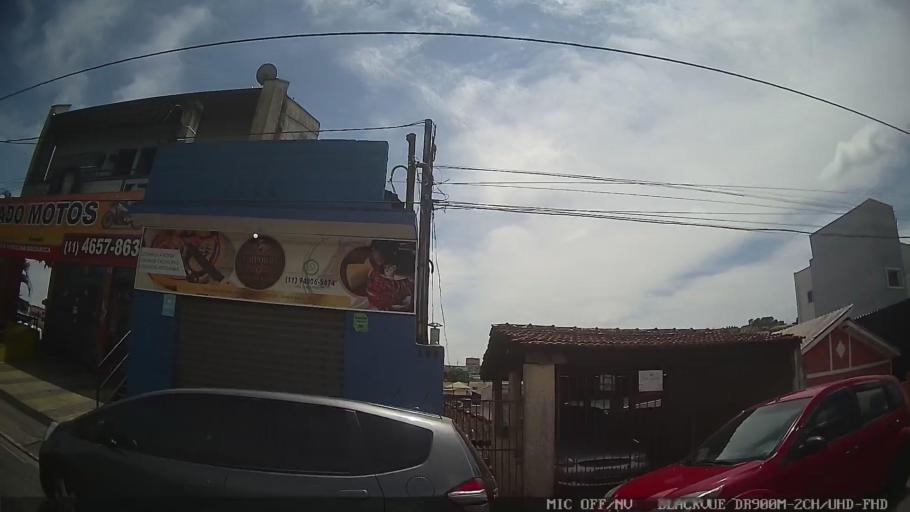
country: BR
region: Sao Paulo
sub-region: Santa Isabel
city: Santa Isabel
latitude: -23.3206
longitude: -46.2255
